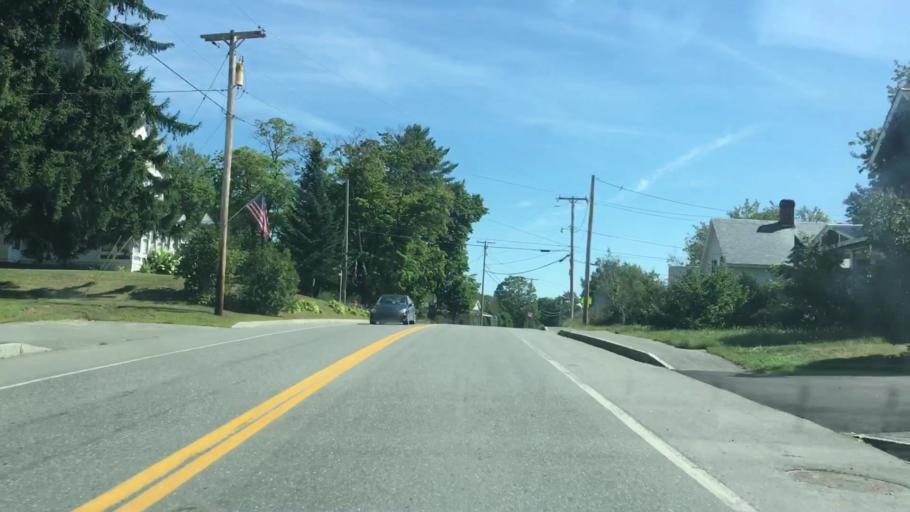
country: US
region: Maine
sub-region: Piscataquis County
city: Milo
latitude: 45.2507
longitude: -68.9827
